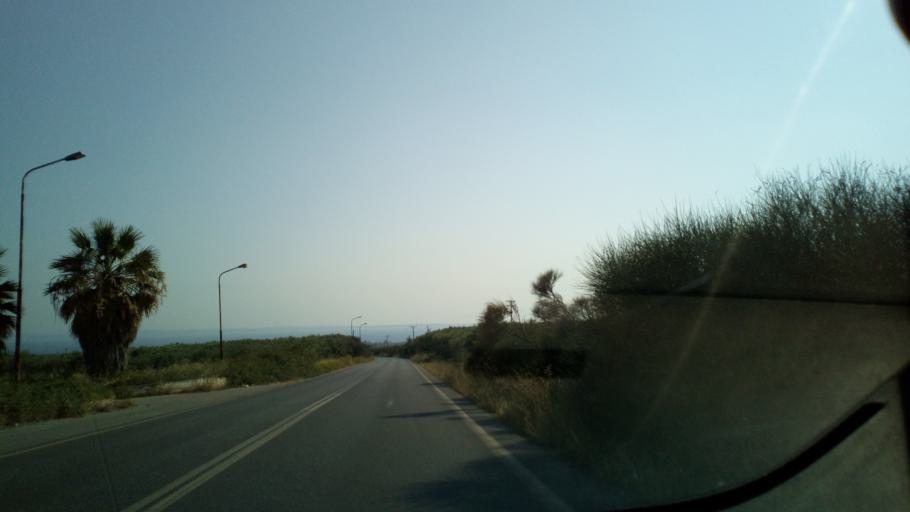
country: GR
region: Central Macedonia
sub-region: Nomos Chalkidikis
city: Kalyves Polygyrou
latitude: 40.3015
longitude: 23.4339
